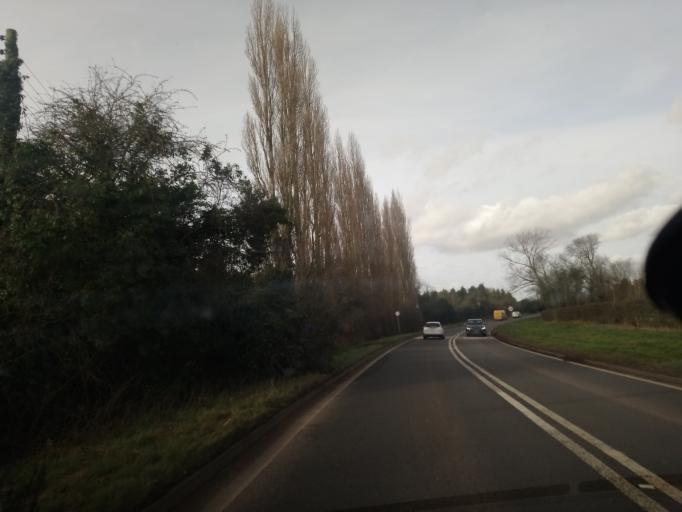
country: GB
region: England
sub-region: Telford and Wrekin
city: Eyton upon the Weald Moors
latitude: 52.7546
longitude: -2.5487
